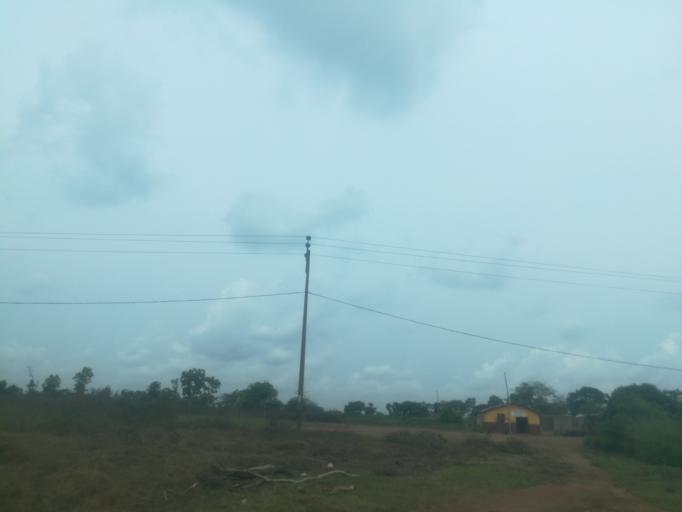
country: NG
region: Ogun
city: Ayetoro
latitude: 7.3568
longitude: 3.0515
